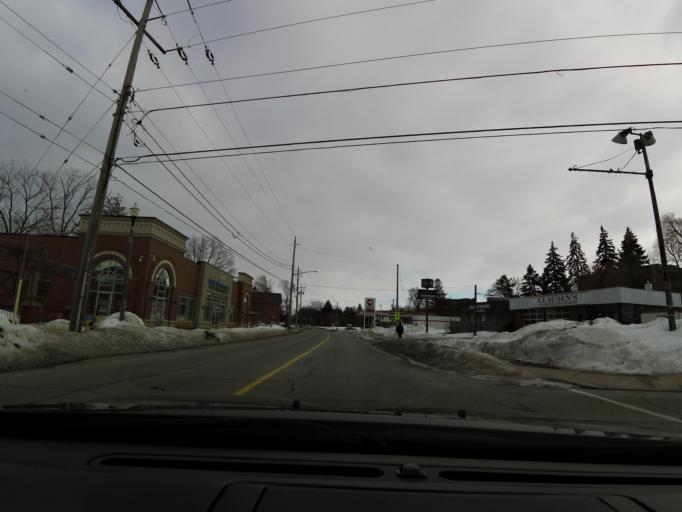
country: CA
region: Ontario
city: Oakville
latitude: 43.1920
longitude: -79.5588
